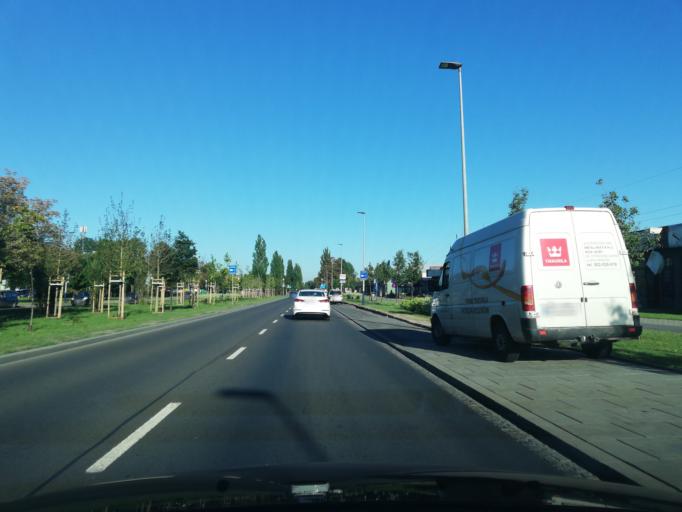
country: PL
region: Lesser Poland Voivodeship
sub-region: Krakow
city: Krakow
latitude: 50.0865
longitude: 20.0096
